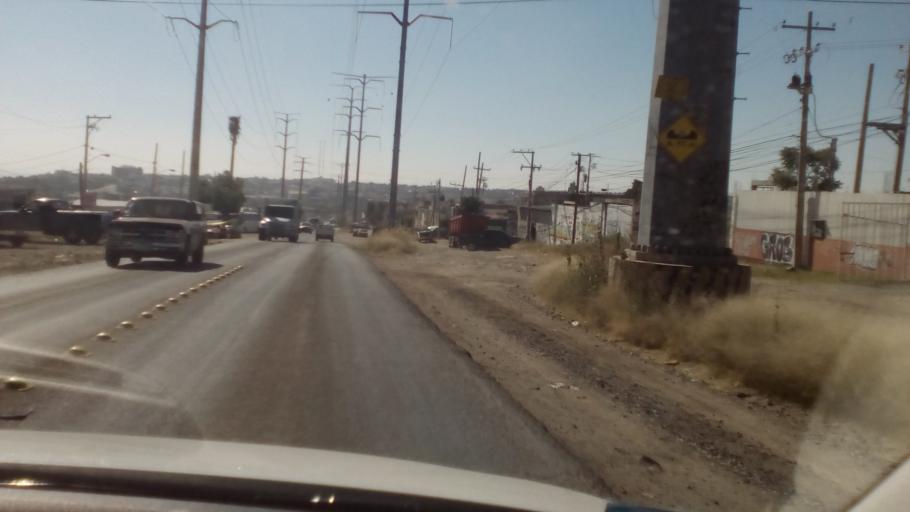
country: MX
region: Guanajuato
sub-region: Leon
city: La Ermita
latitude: 21.1434
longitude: -101.7263
